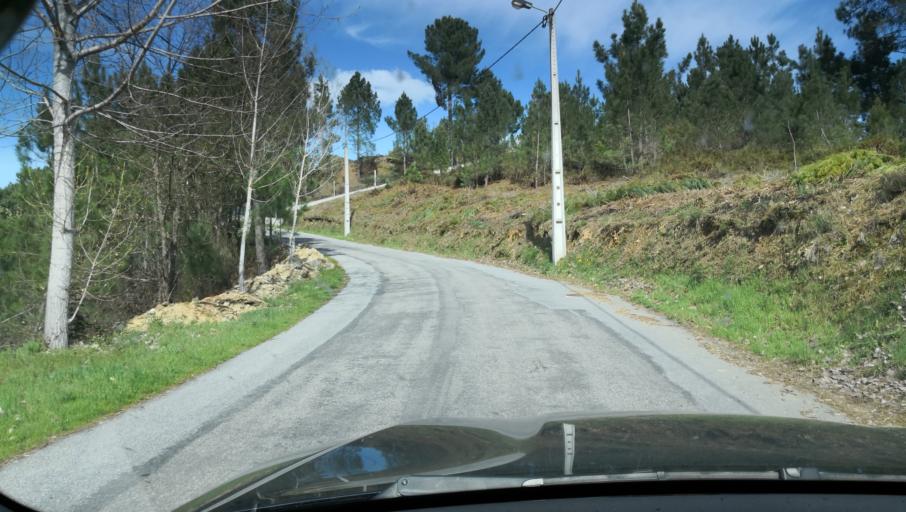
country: PT
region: Vila Real
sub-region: Vila Real
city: Vila Real
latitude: 41.2536
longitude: -7.6828
